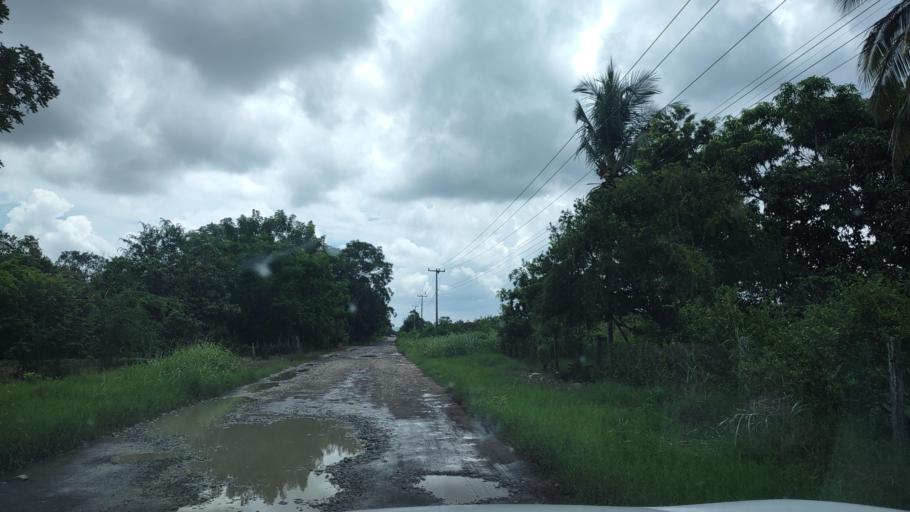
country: MX
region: Veracruz
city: Alamo
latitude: 20.9540
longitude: -97.7046
